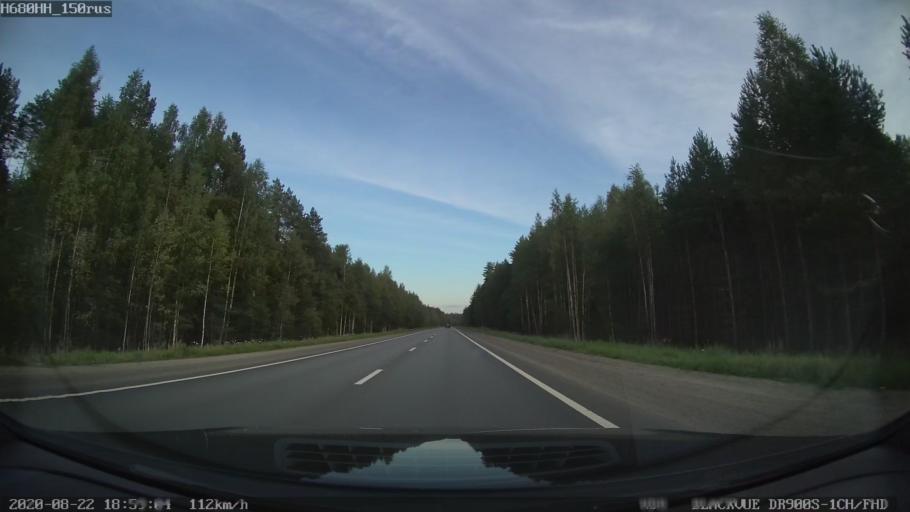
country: RU
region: Tverskaya
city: Rameshki
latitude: 57.1475
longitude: 36.0872
